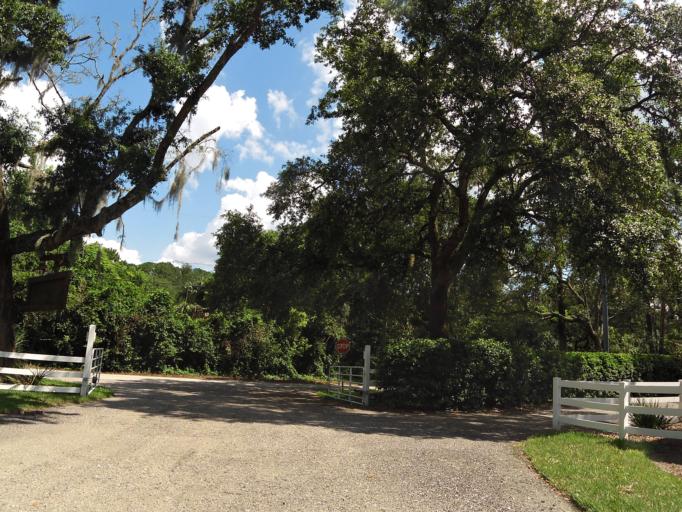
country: US
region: Florida
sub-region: Saint Johns County
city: Palm Valley
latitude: 30.1473
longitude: -81.5134
